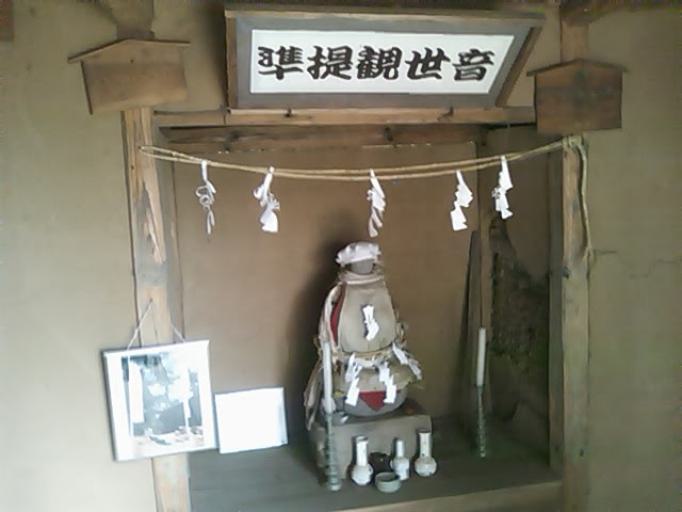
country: JP
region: Nagano
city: Komoro
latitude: 36.3587
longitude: 138.4249
